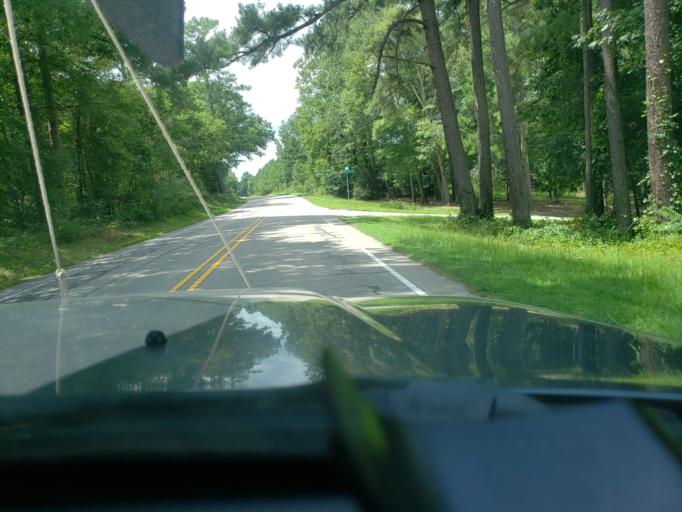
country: US
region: North Carolina
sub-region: Wake County
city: Rolesville
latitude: 35.8779
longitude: -78.4641
